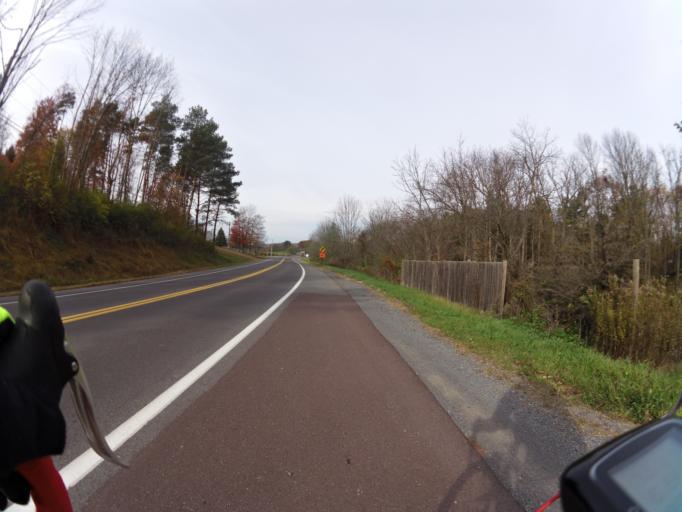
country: US
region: Pennsylvania
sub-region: Union County
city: New Columbia
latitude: 41.0442
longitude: -76.8785
